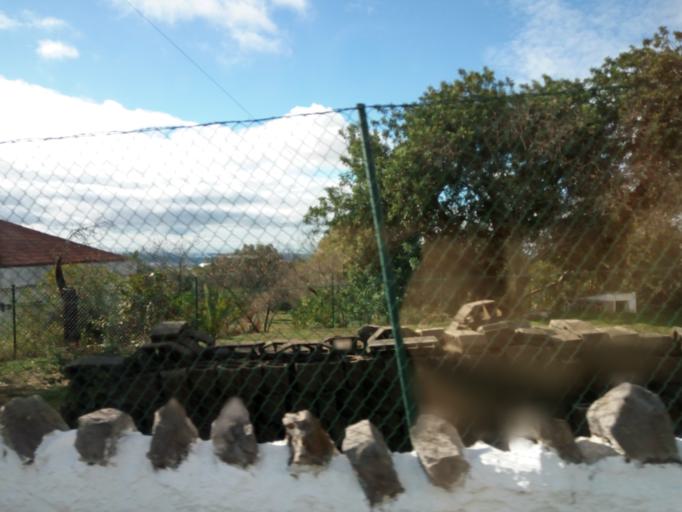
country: PT
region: Faro
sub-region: Faro
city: Santa Barbara de Nexe
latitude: 37.1095
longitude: -7.9628
